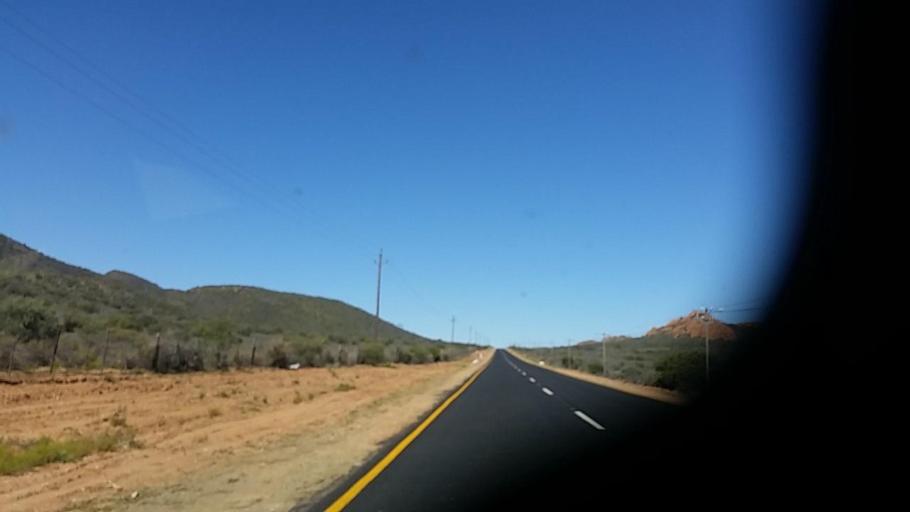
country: ZA
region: Western Cape
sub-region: Eden District Municipality
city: Oudtshoorn
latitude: -33.4866
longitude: 22.5709
